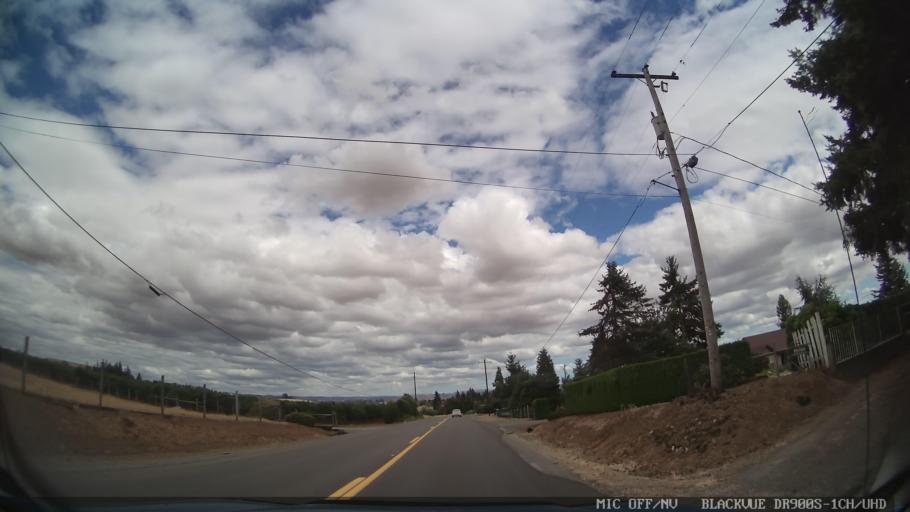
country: US
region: Oregon
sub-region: Marion County
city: Aumsville
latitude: 44.8604
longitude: -122.8547
